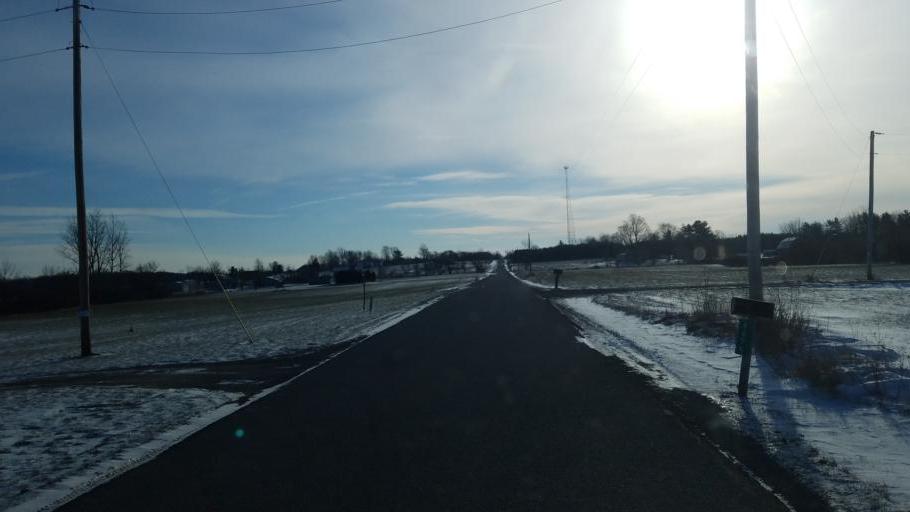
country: US
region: Ohio
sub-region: Morrow County
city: Mount Gilead
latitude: 40.6249
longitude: -82.7942
